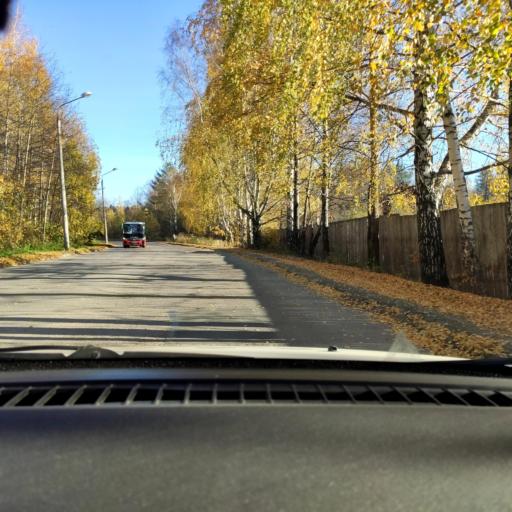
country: RU
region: Perm
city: Perm
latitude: 58.0800
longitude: 56.3676
